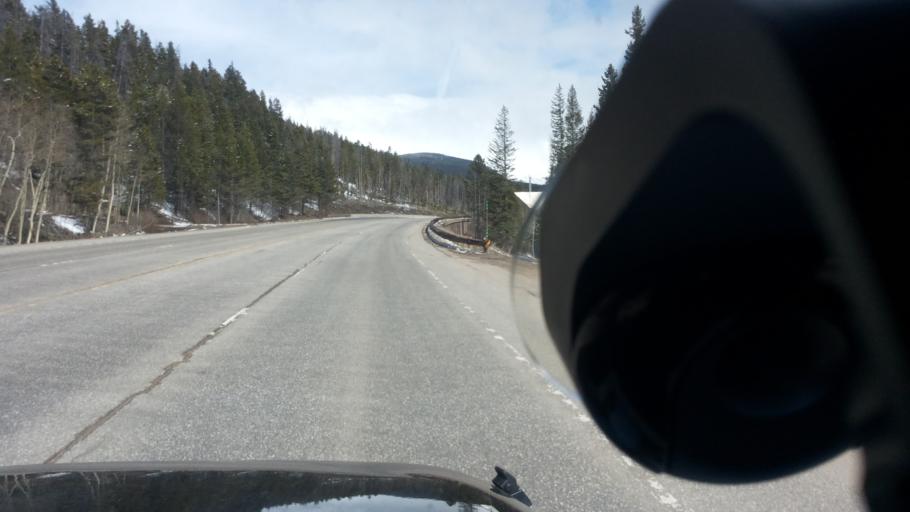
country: US
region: Colorado
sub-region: Grand County
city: Fraser
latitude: 39.8980
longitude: -105.7712
